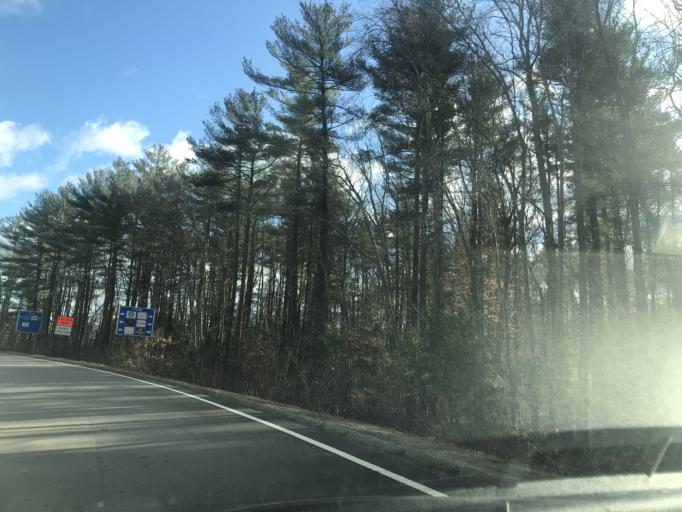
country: US
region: Massachusetts
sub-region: Plymouth County
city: Hanover
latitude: 42.1499
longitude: -70.8474
